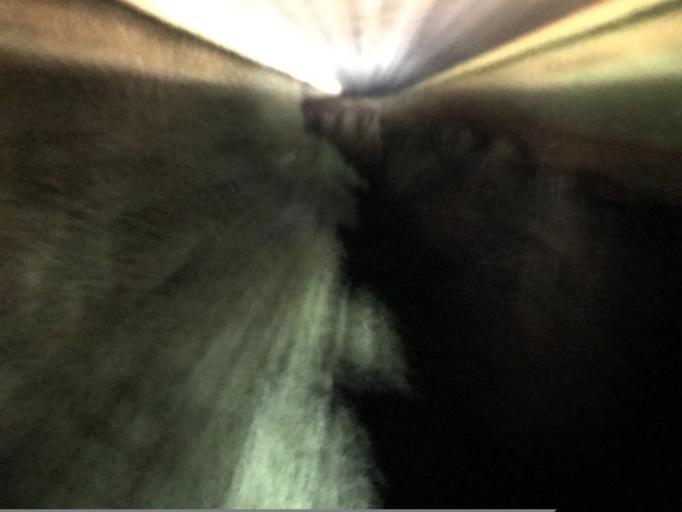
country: FR
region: Auvergne
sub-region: Departement du Puy-de-Dome
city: Saint-Remy-sur-Durolle
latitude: 45.9481
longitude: 3.6404
